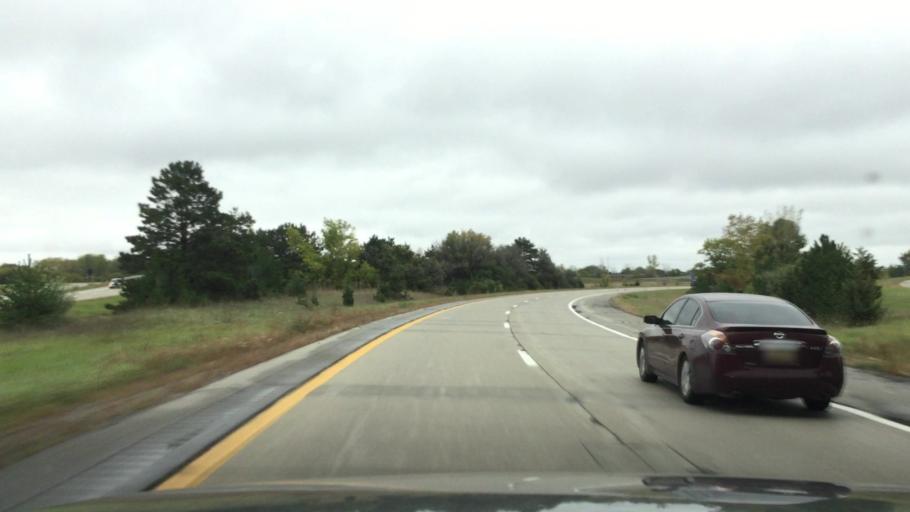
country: US
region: Michigan
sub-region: Saginaw County
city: Buena Vista
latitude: 43.4339
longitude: -83.8963
